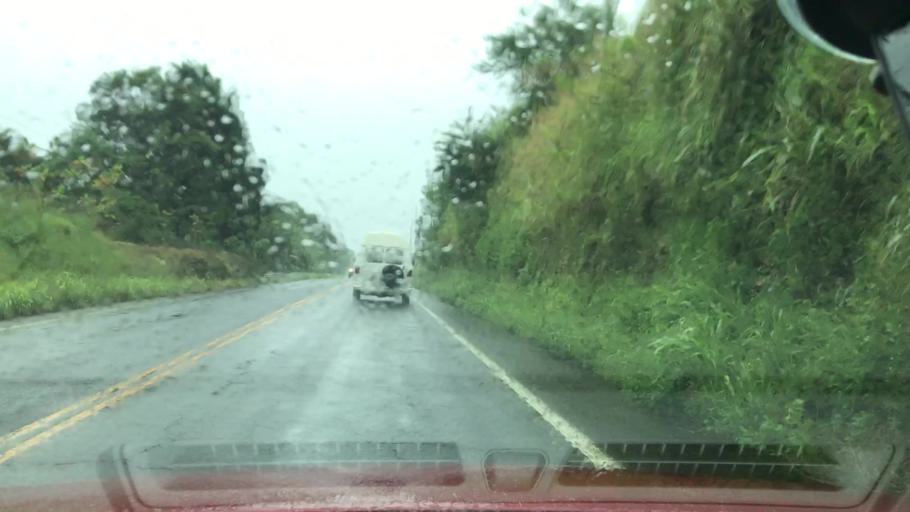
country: US
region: Hawaii
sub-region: Hawaii County
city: Pepeekeo
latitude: 19.9858
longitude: -155.2399
